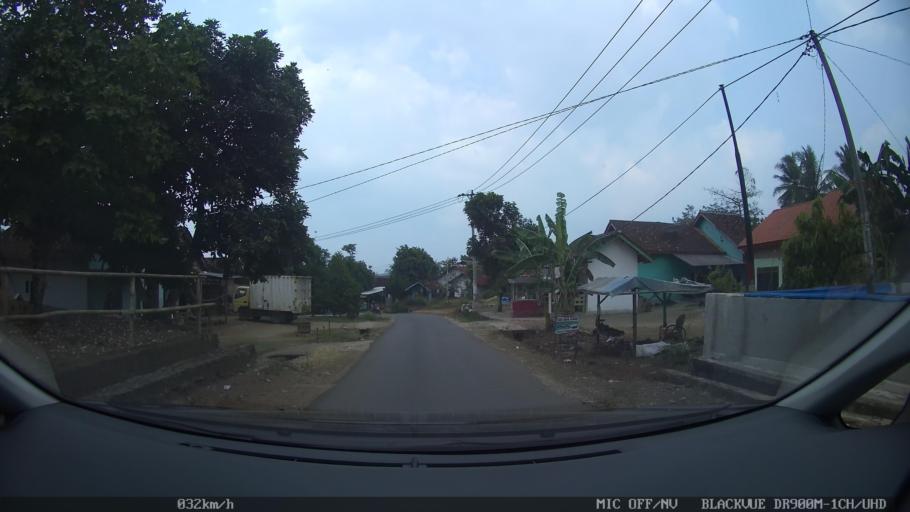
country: ID
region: Lampung
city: Gadingrejo
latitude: -5.3910
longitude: 105.0412
